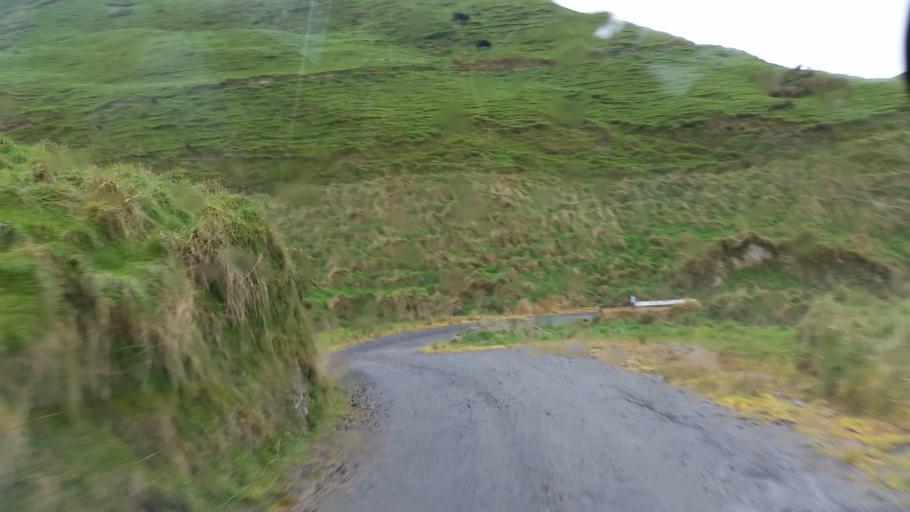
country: NZ
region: Taranaki
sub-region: South Taranaki District
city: Eltham
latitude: -39.4763
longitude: 174.4105
